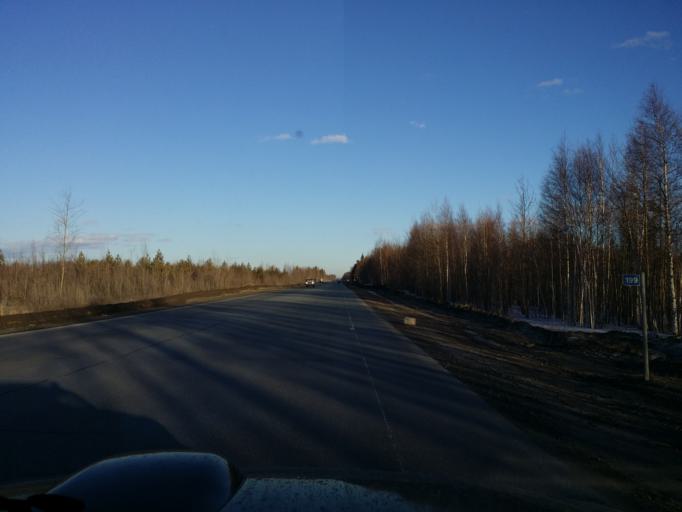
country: RU
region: Khanty-Mansiyskiy Avtonomnyy Okrug
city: Megion
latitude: 61.0671
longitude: 76.2549
